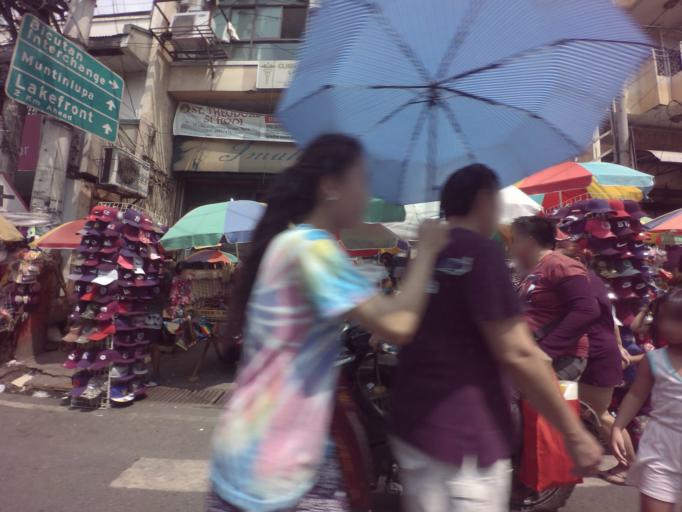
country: PH
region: Calabarzon
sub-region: Province of Rizal
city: Taguig
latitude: 14.4893
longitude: 121.0610
